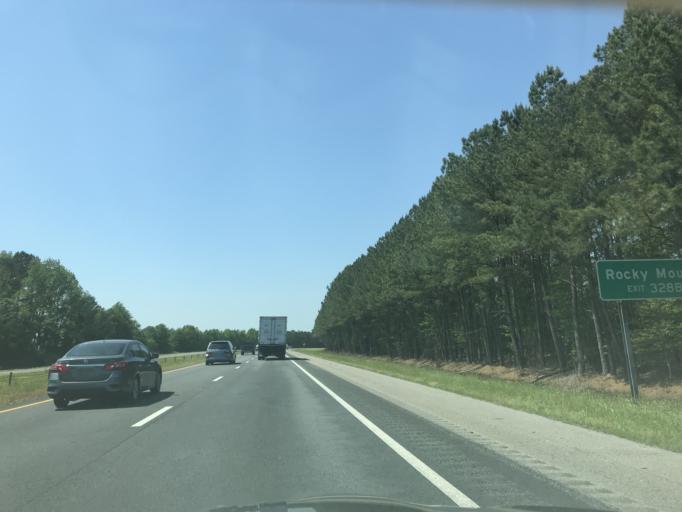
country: US
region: North Carolina
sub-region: Johnston County
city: Benson
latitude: 35.3702
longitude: -78.4977
